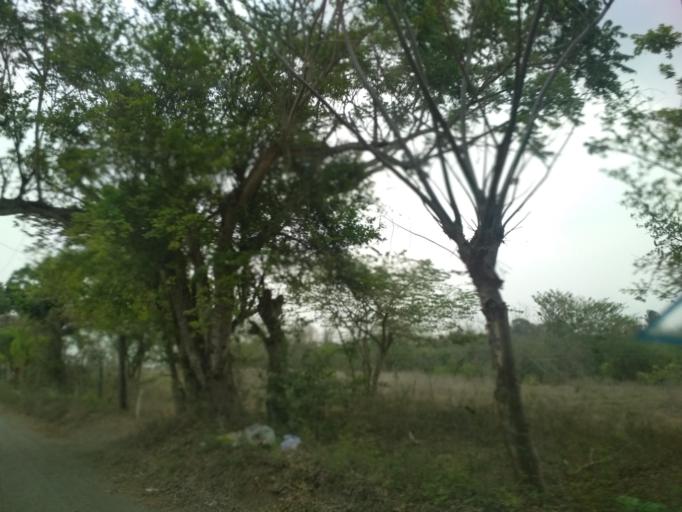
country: MX
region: Veracruz
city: Paso del Toro
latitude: 19.0268
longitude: -96.1491
